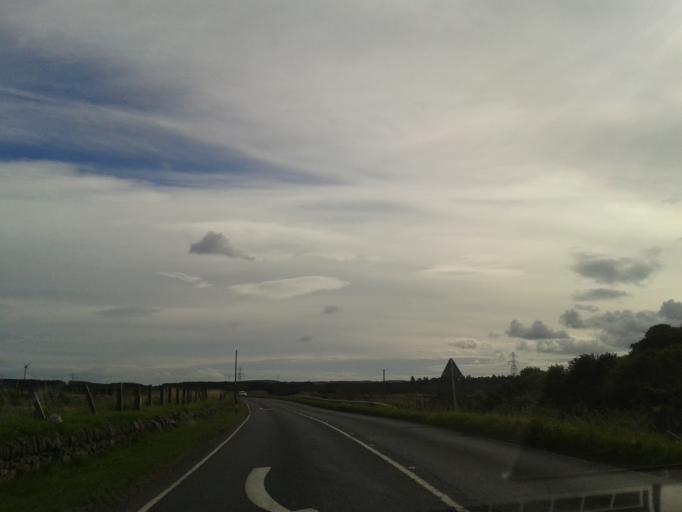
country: GB
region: Scotland
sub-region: Aberdeenshire
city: Portsoy
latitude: 57.6718
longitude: -2.6830
